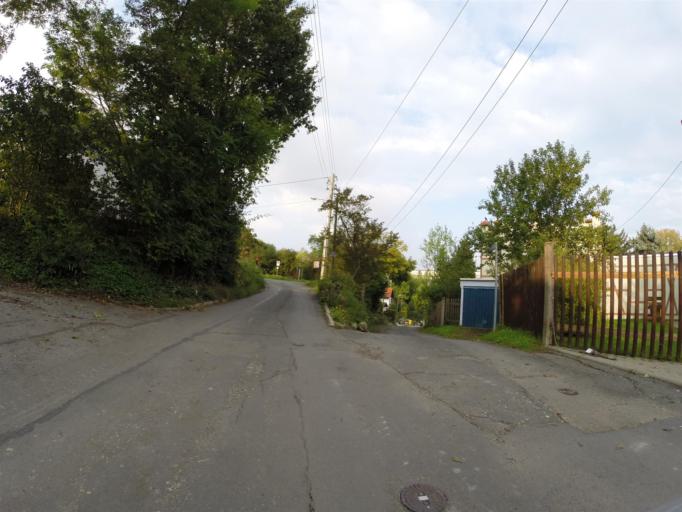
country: DE
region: Thuringia
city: Jena
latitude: 50.9155
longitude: 11.5622
